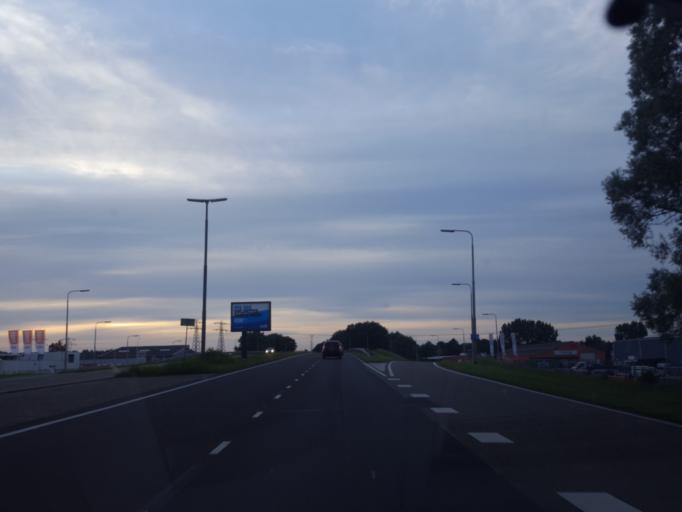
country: NL
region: Friesland
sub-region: Gemeente Leeuwarden
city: Camminghaburen
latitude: 53.1971
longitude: 5.8394
